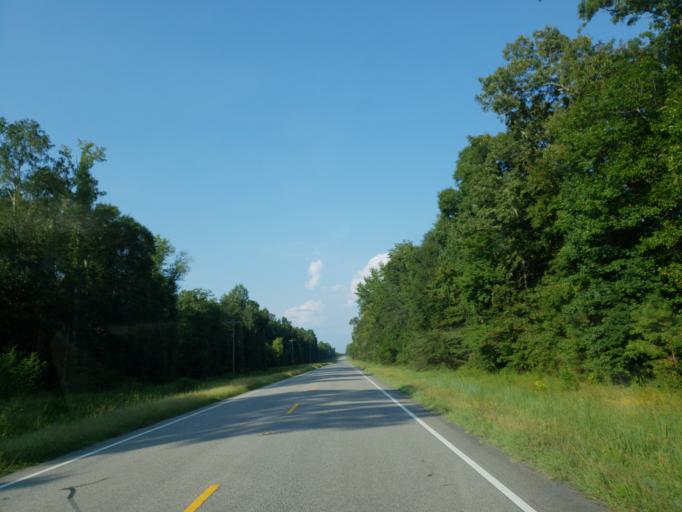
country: US
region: Alabama
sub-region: Greene County
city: Eutaw
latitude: 32.7355
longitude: -88.0559
